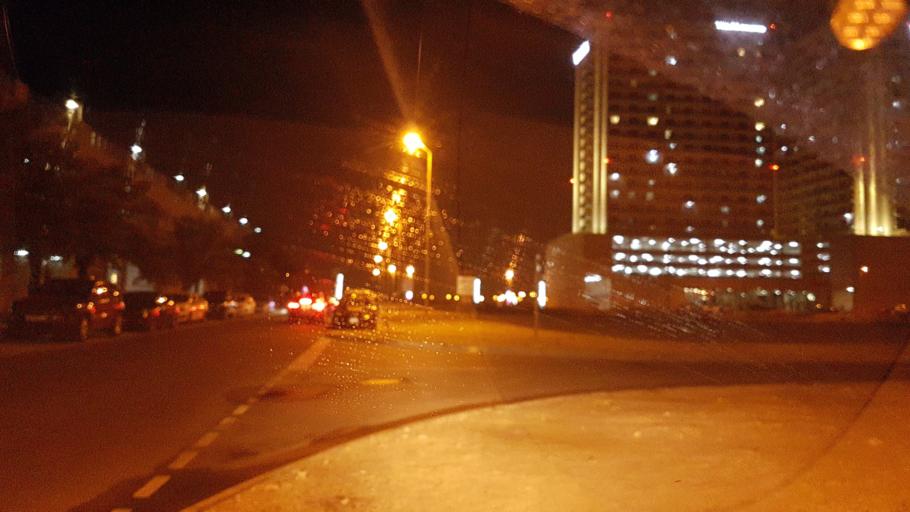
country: BH
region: Muharraq
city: Al Hadd
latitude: 26.2882
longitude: 50.6622
